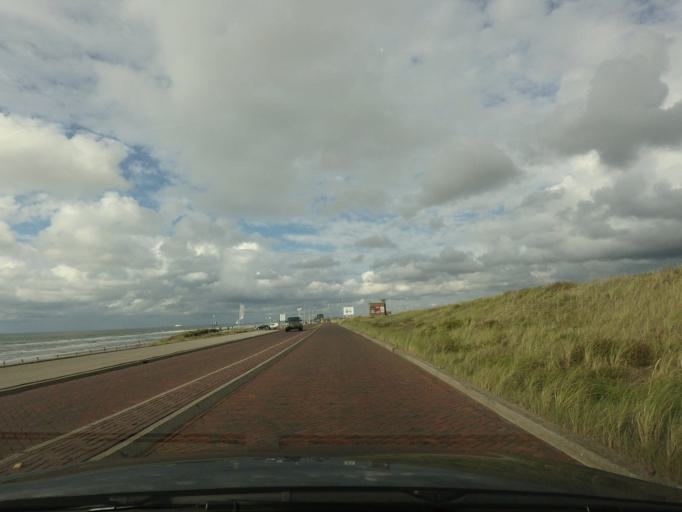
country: NL
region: North Holland
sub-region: Gemeente Zandvoort
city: Zandvoort
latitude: 52.3927
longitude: 4.5385
